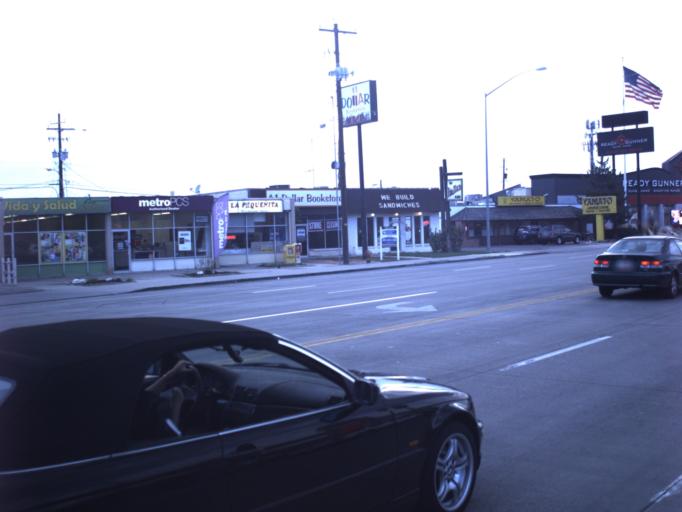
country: US
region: Utah
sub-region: Utah County
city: Orem
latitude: 40.2767
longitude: -111.6859
